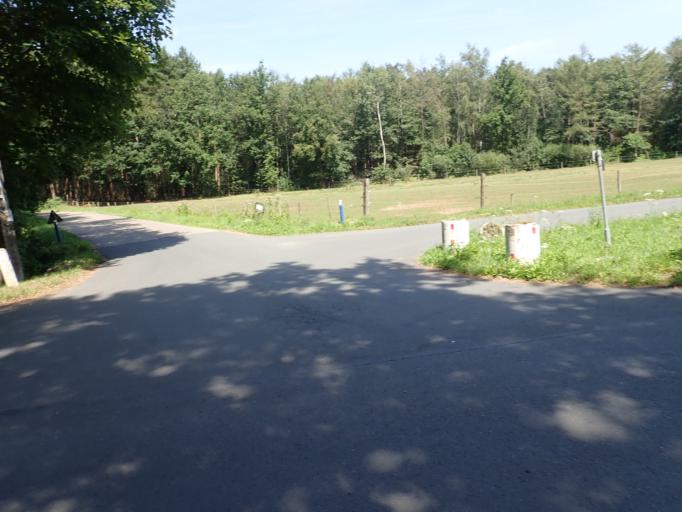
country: BE
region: Flanders
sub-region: Provincie Antwerpen
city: Zandhoven
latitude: 51.2239
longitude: 4.6433
